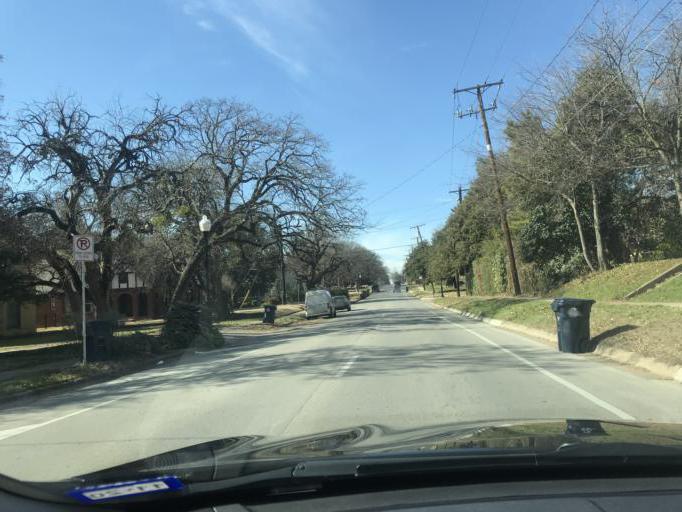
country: US
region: Texas
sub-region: Denton County
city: Denton
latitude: 33.2156
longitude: -97.1383
